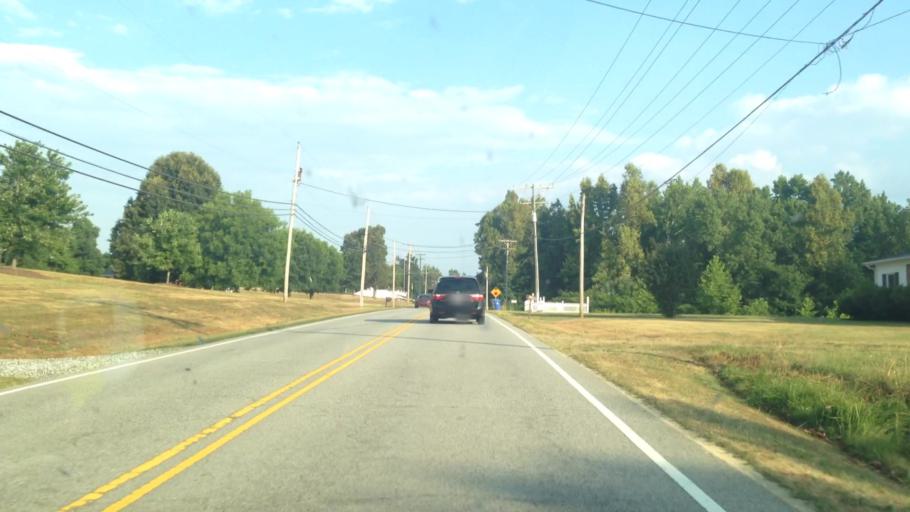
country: US
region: North Carolina
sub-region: Davidson County
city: Thomasville
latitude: 35.9422
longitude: -80.0739
